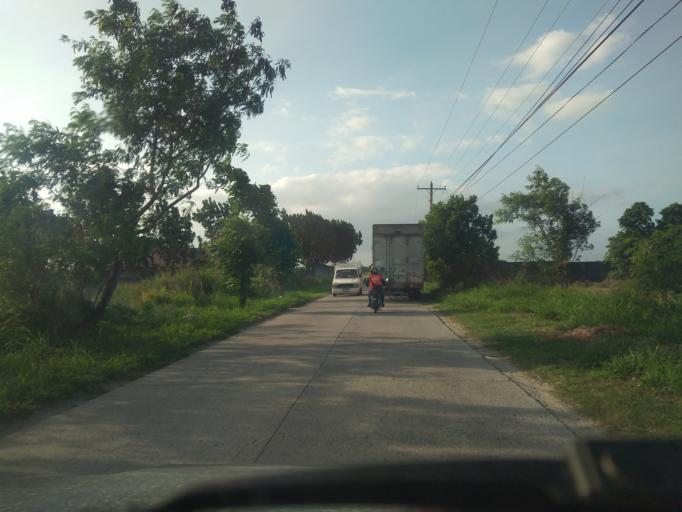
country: PH
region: Central Luzon
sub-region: Province of Pampanga
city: Malino
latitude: 15.1082
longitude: 120.6698
